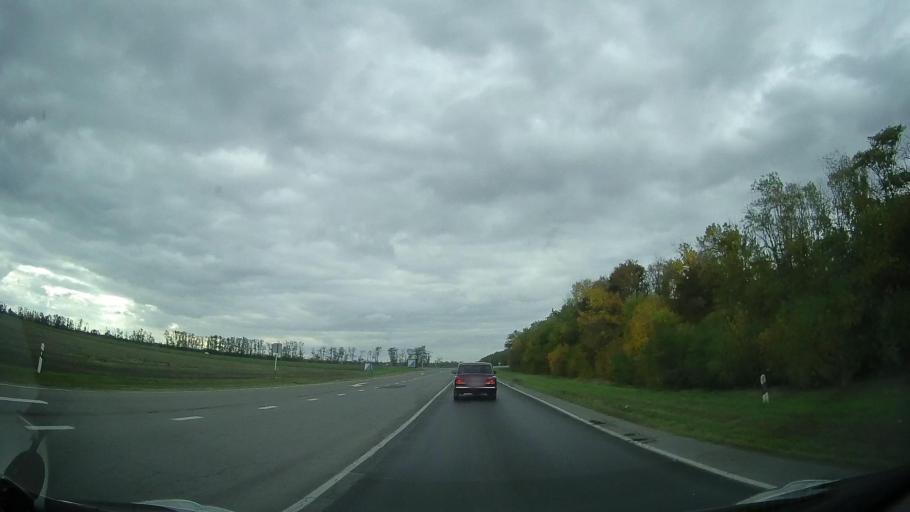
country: RU
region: Rostov
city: Yegorlykskaya
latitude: 46.5368
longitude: 40.7866
